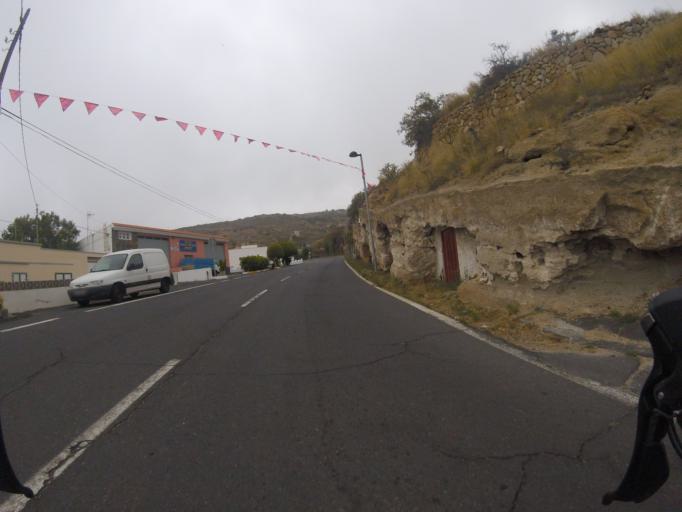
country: ES
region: Canary Islands
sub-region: Provincia de Santa Cruz de Tenerife
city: Guimar
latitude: 28.2842
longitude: -16.4061
